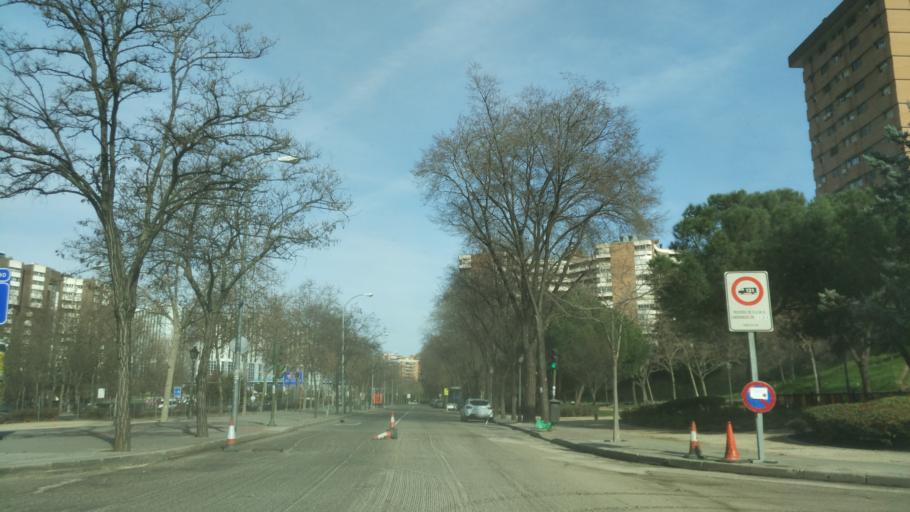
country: ES
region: Madrid
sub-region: Provincia de Madrid
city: Tetuan de las Victorias
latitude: 40.4836
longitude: -3.6993
